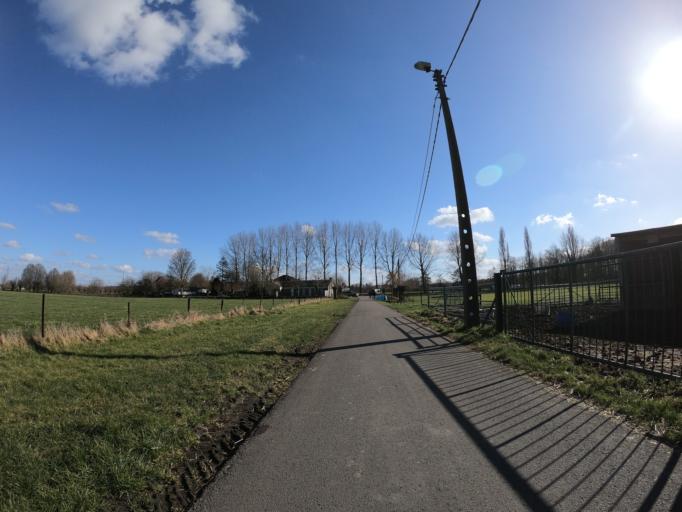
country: BE
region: Flanders
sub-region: Provincie West-Vlaanderen
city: Avelgem
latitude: 50.7720
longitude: 3.4535
